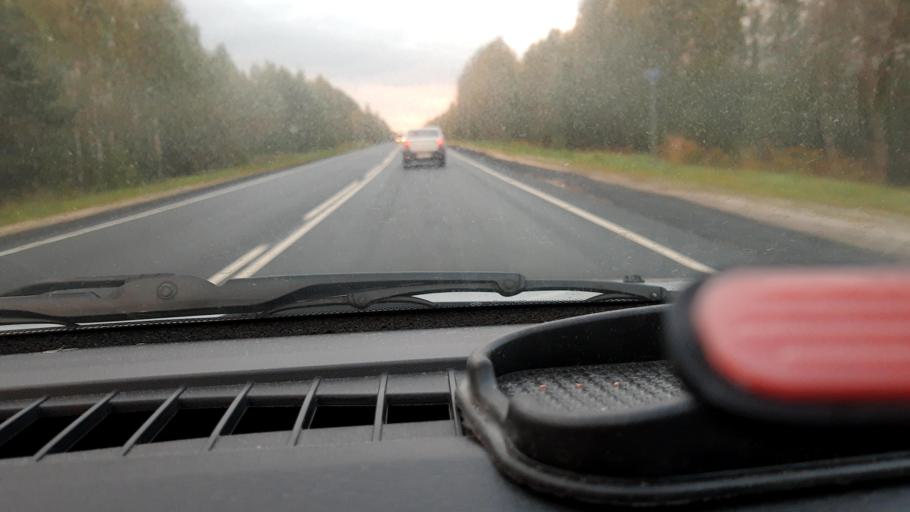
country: RU
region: Nizjnij Novgorod
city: Semenov
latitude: 56.7747
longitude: 44.4239
